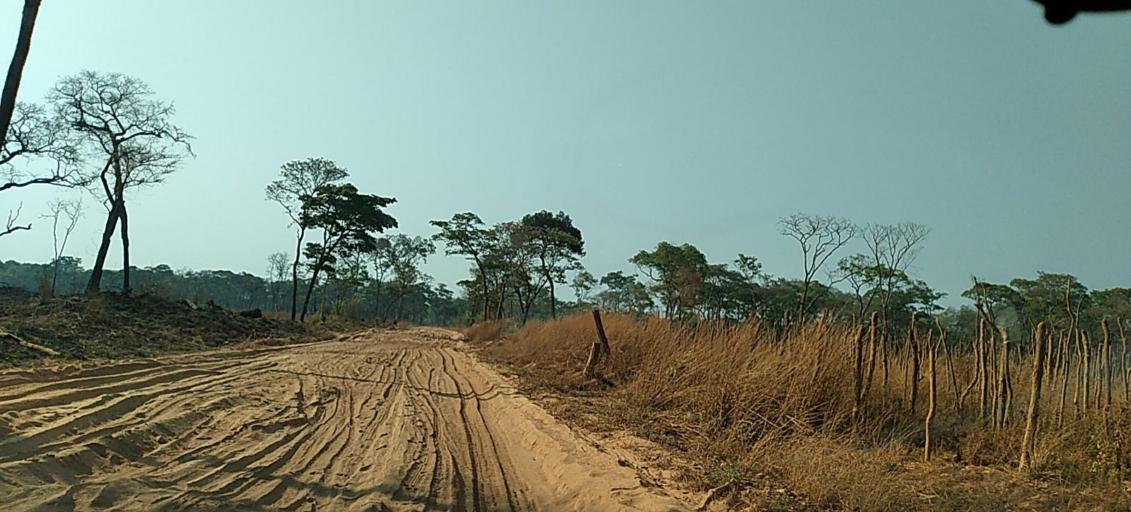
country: ZM
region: North-Western
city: Kasempa
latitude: -13.6232
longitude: 25.9822
